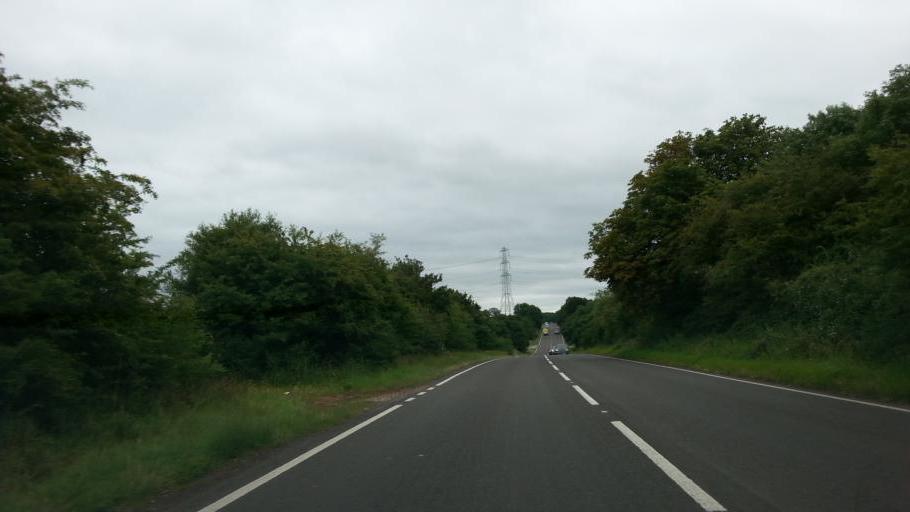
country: GB
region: England
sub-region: Nottinghamshire
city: Farndon
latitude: 53.1257
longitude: -0.8798
